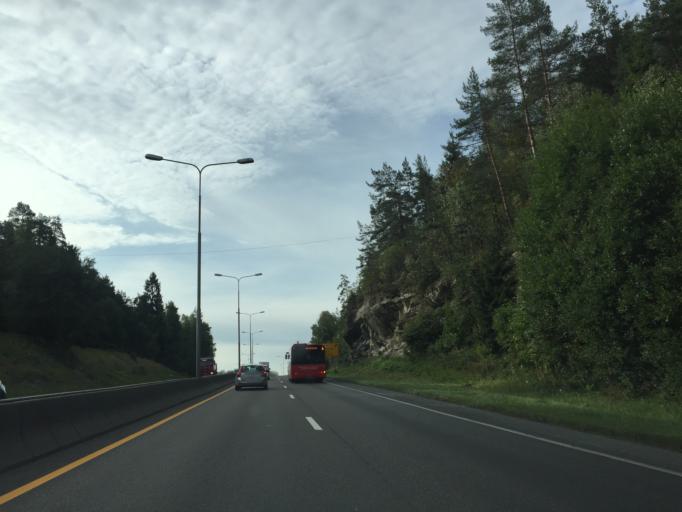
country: NO
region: Akershus
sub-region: Oppegard
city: Kolbotn
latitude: 59.8537
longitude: 10.8333
